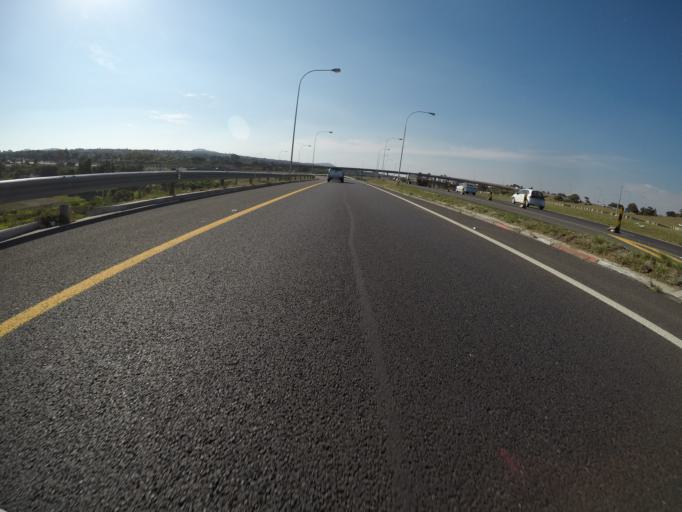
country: ZA
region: Western Cape
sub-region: City of Cape Town
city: Kraaifontein
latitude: -33.8754
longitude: 18.6715
